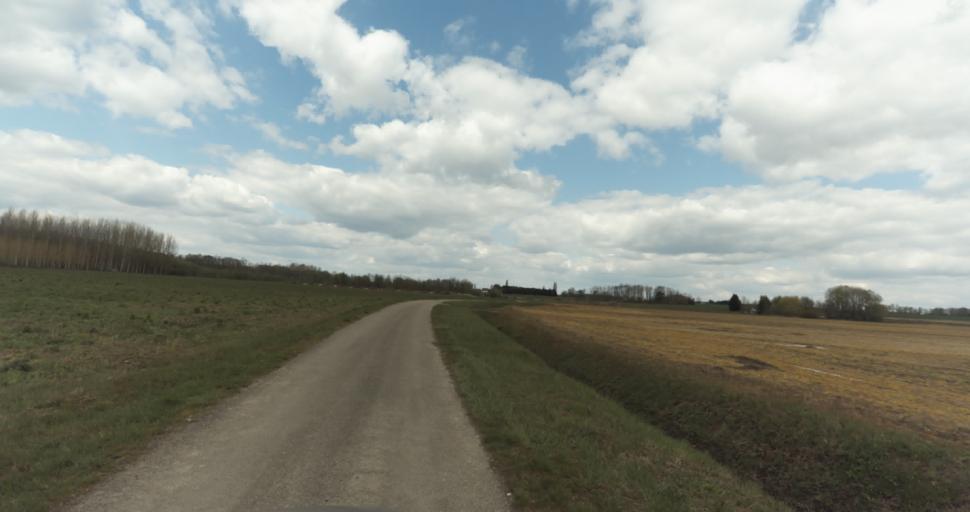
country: FR
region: Bourgogne
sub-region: Departement de la Cote-d'Or
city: Auxonne
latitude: 47.1684
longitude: 5.3941
